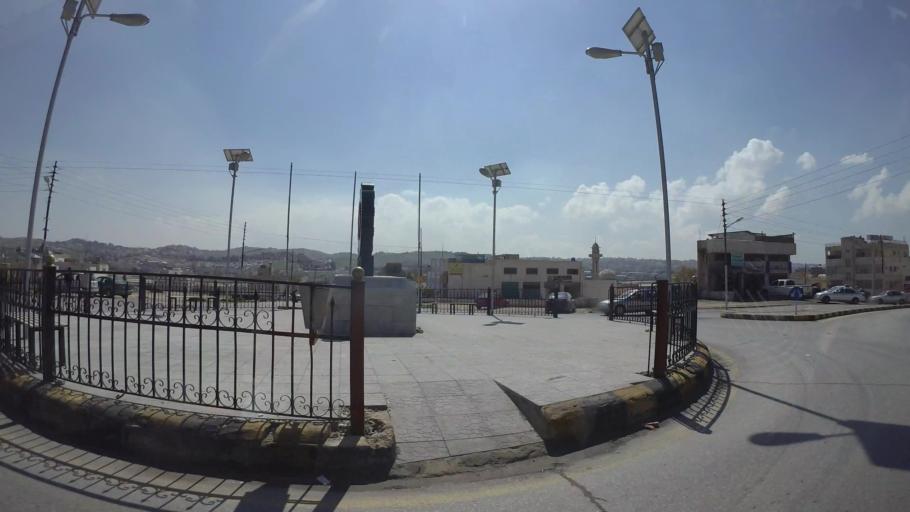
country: JO
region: Amman
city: Amman
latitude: 31.9809
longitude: 35.9979
